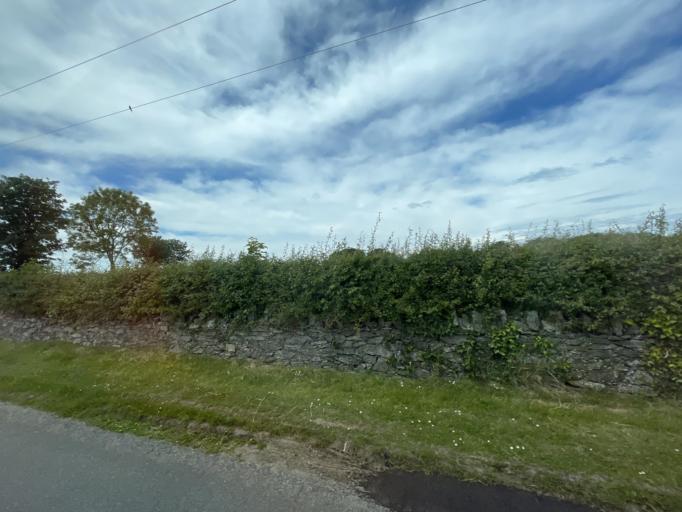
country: GB
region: Wales
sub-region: Anglesey
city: Gaerwen
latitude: 53.2136
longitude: -4.2505
